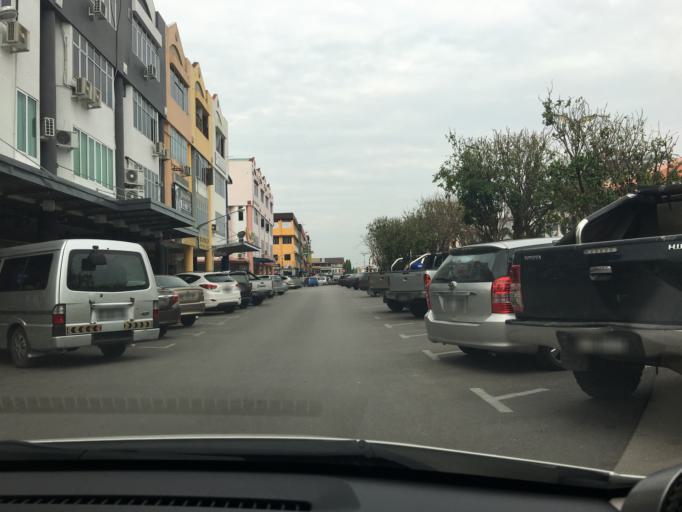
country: MY
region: Sarawak
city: Sarikei
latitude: 2.1307
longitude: 111.5187
